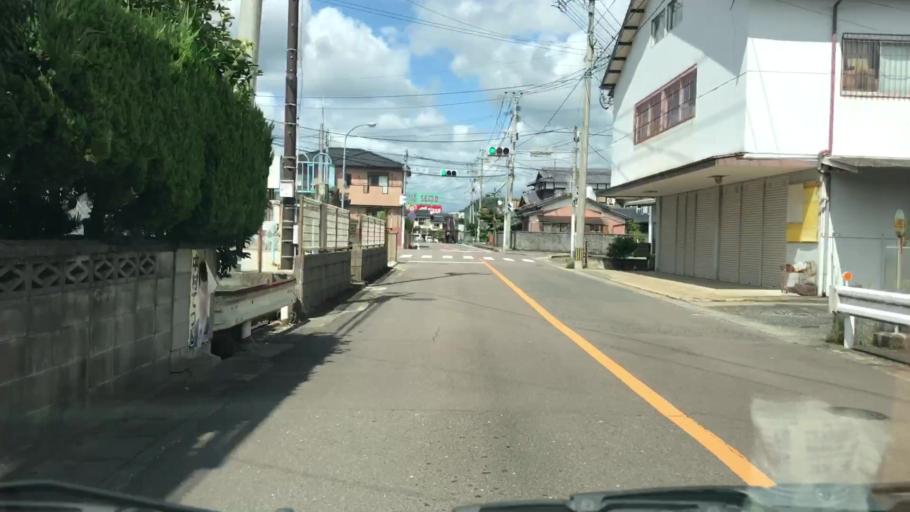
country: JP
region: Saga Prefecture
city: Saga-shi
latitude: 33.2458
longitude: 130.2033
